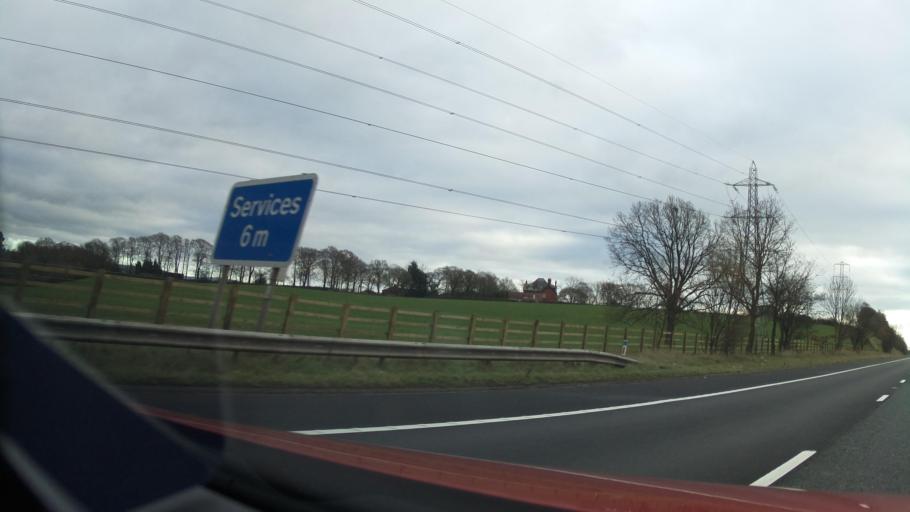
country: GB
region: England
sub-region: Cumbria
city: Scotby
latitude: 54.8856
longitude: -2.8840
